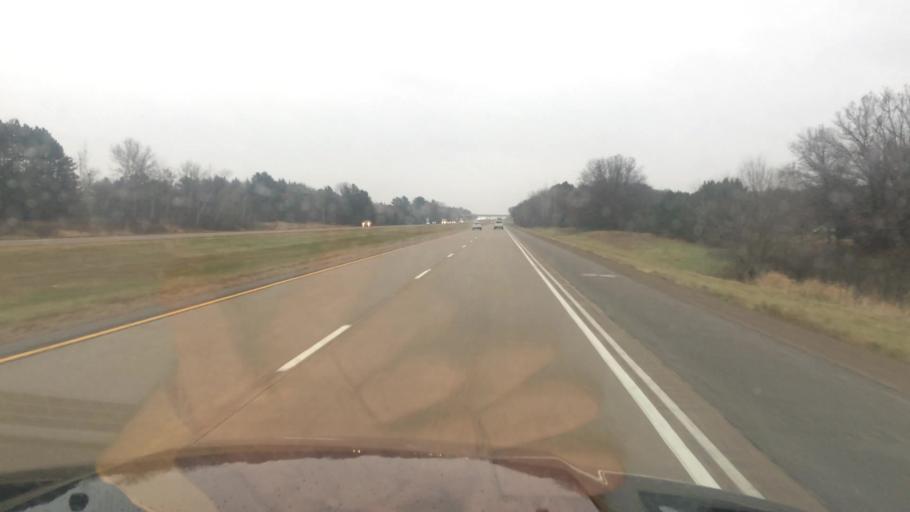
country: US
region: Wisconsin
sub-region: Portage County
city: Stevens Point
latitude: 44.6095
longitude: -89.6224
